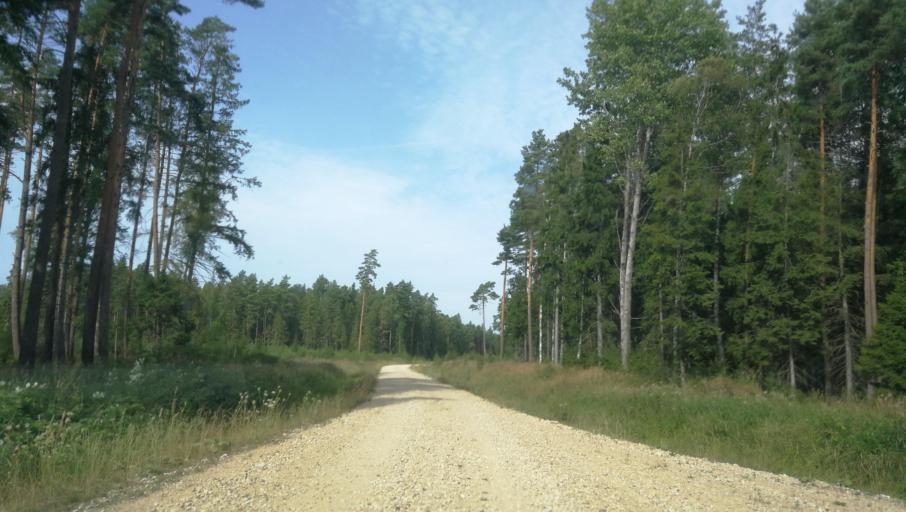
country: LV
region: Pavilostas
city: Pavilosta
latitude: 56.8146
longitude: 21.3351
